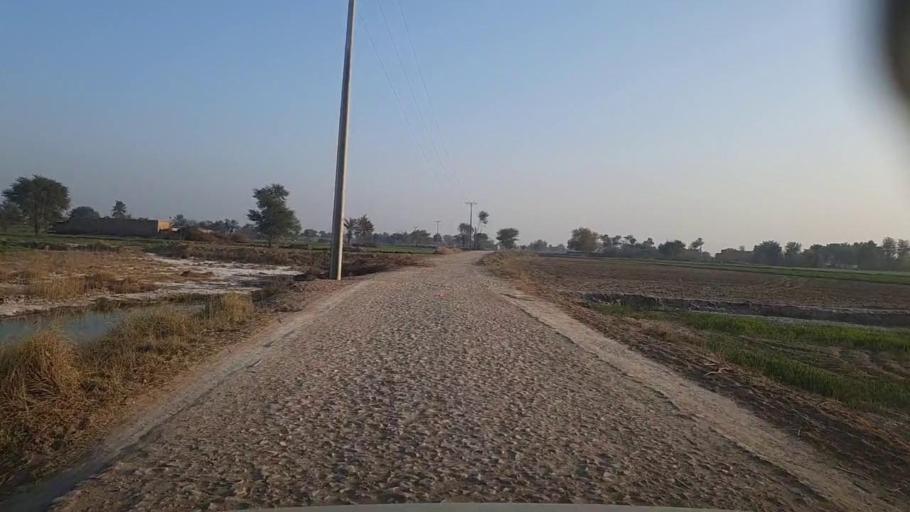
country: PK
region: Sindh
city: Khairpur
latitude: 28.0634
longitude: 69.7534
